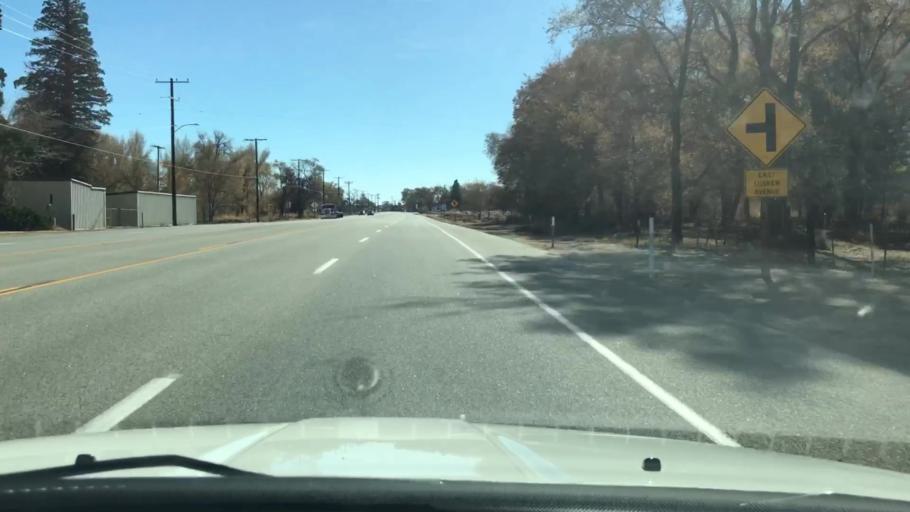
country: US
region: California
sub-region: Inyo County
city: Lone Pine
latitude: 36.6138
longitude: -118.0664
